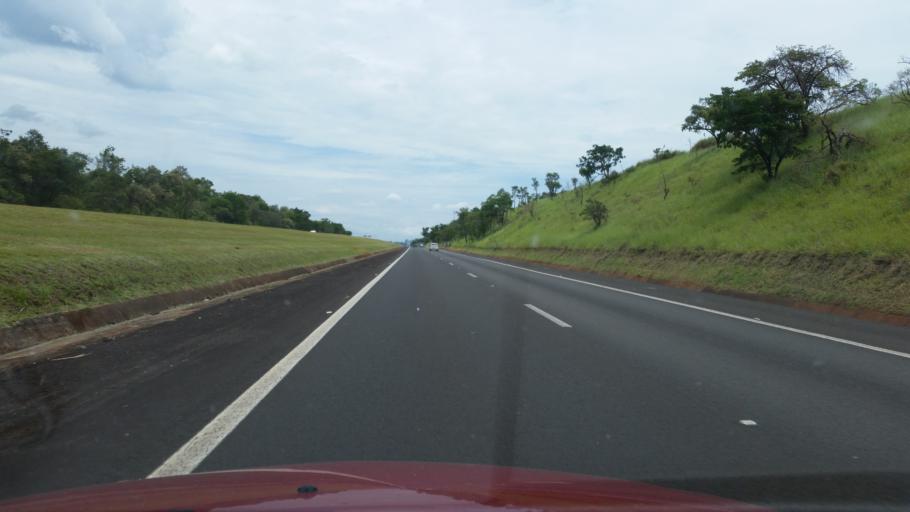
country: BR
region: Sao Paulo
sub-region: Avare
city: Avare
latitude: -22.9732
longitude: -48.7911
